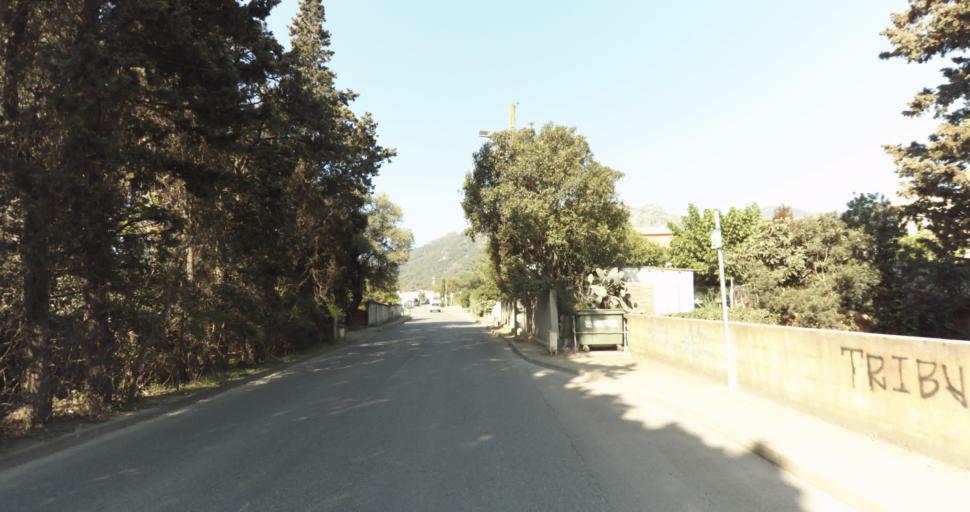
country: FR
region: Corsica
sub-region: Departement de la Haute-Corse
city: Biguglia
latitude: 42.6298
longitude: 9.4357
